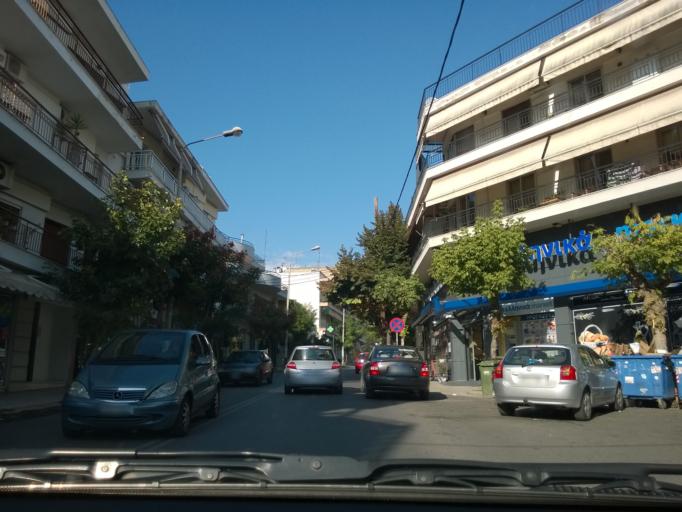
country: GR
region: Central Macedonia
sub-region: Nomos Thessalonikis
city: Polichni
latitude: 40.6624
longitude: 22.9470
